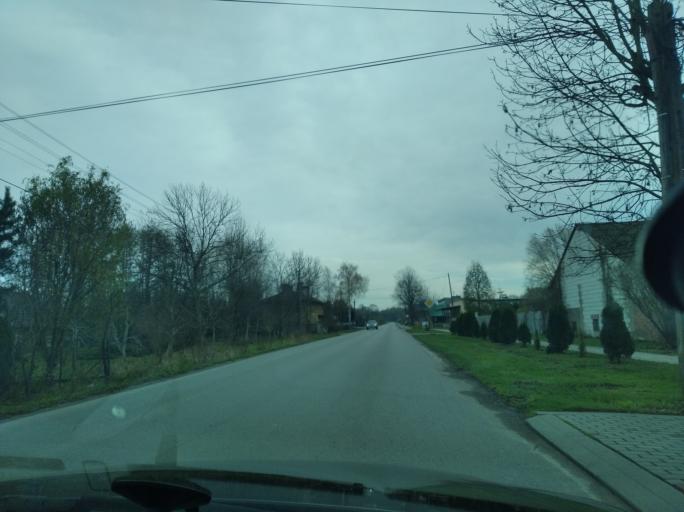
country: PL
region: Subcarpathian Voivodeship
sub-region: Powiat przeworski
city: Gac
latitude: 50.0284
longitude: 22.3715
